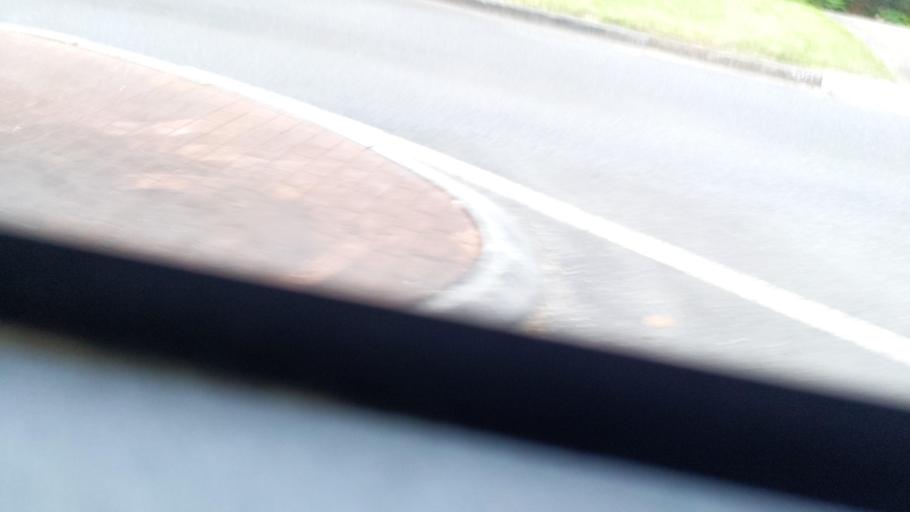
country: AU
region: New South Wales
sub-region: The Hills Shire
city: Baulkham Hills
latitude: -33.7535
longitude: 150.9606
